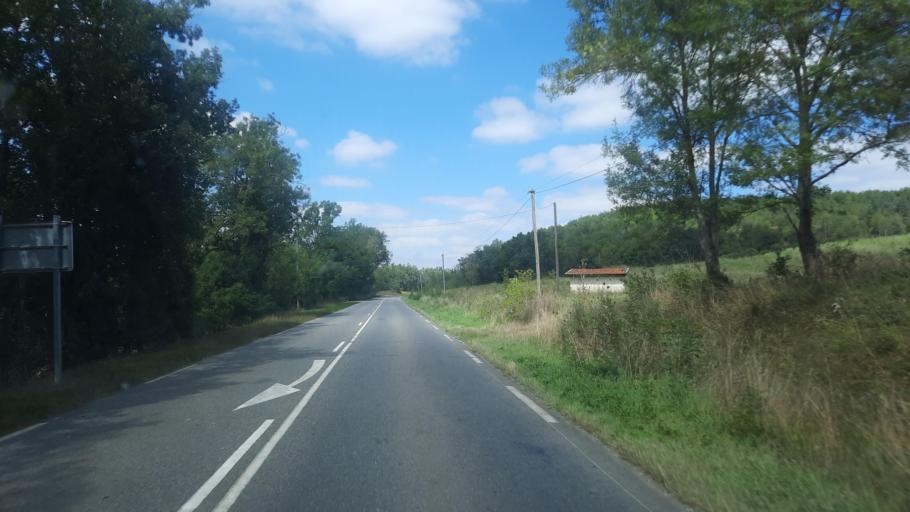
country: FR
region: Midi-Pyrenees
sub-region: Departement du Gers
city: Samatan
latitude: 43.5004
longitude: 0.9709
